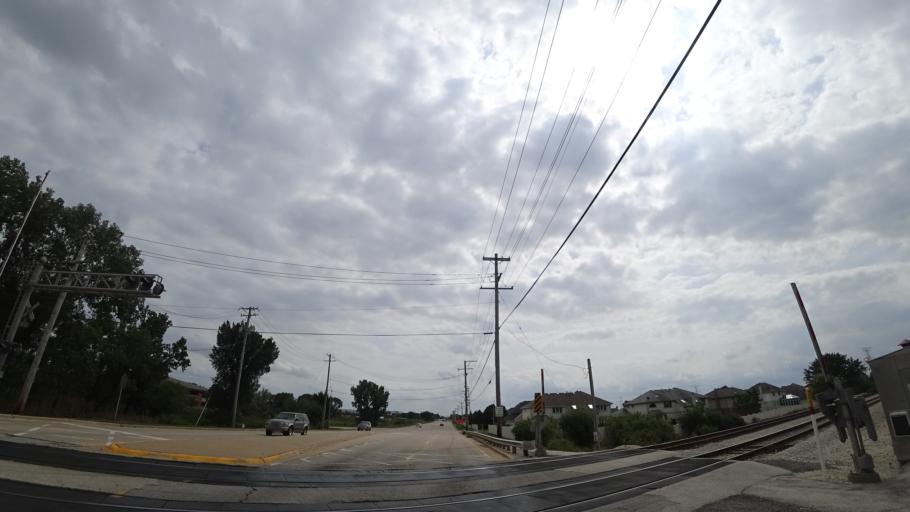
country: US
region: Illinois
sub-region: Cook County
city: Tinley Park
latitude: 41.5633
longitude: -87.8125
